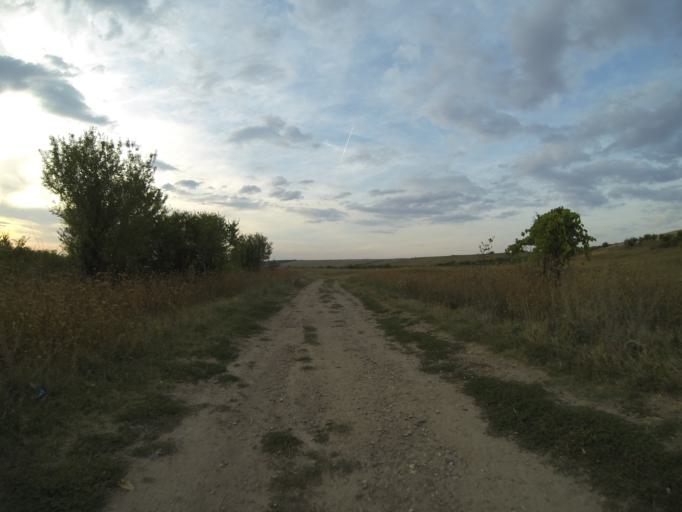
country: RO
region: Dolj
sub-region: Comuna Ceratu
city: Ceratu
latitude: 44.0878
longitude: 23.6698
